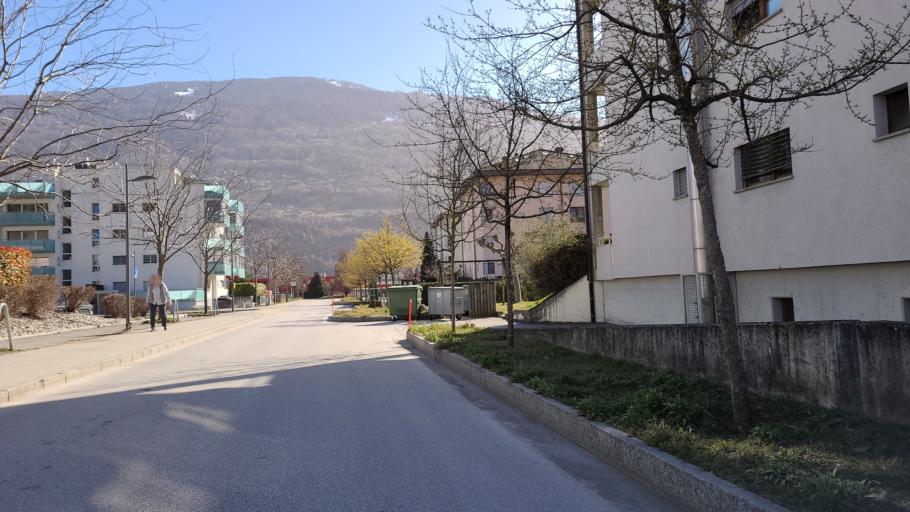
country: CH
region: Valais
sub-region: Sion District
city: Sitten
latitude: 46.2248
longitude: 7.3369
